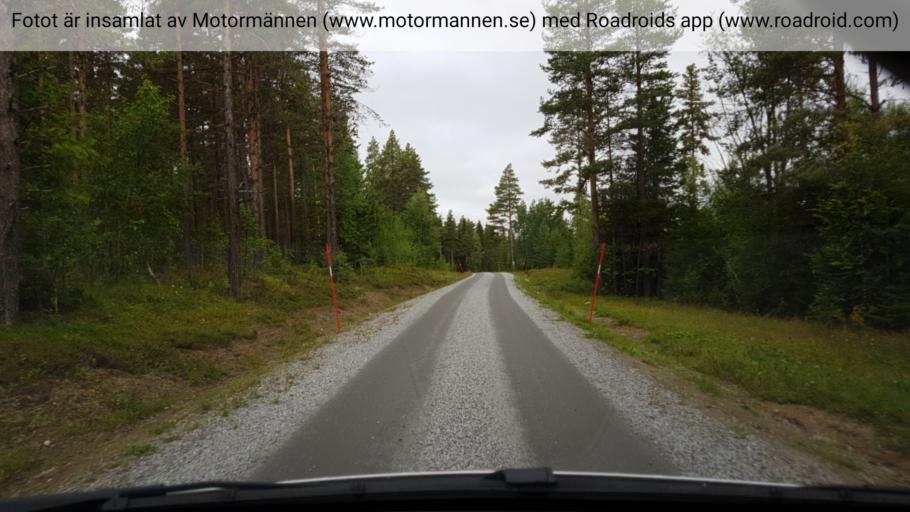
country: SE
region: Vaesterbotten
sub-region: Dorotea Kommun
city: Dorotea
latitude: 63.8363
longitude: 16.3729
